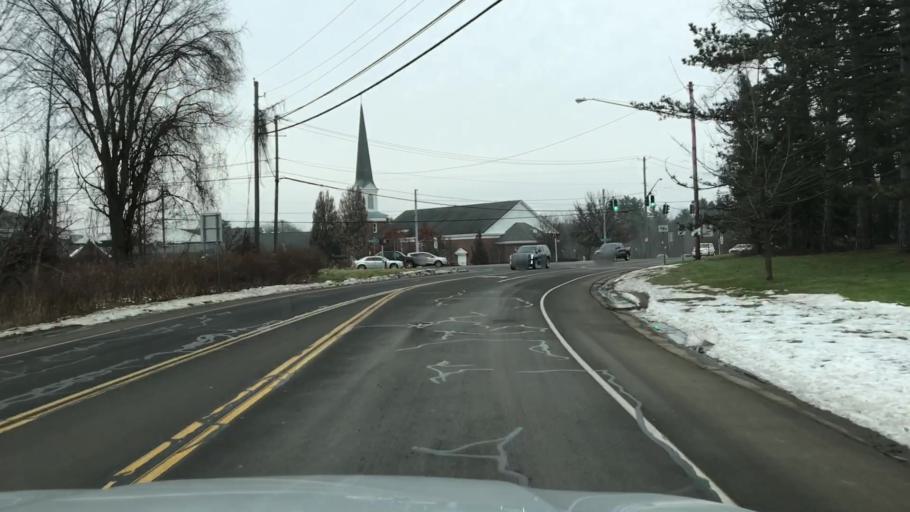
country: US
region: New York
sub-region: Erie County
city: Hamburg
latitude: 42.7514
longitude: -78.8132
